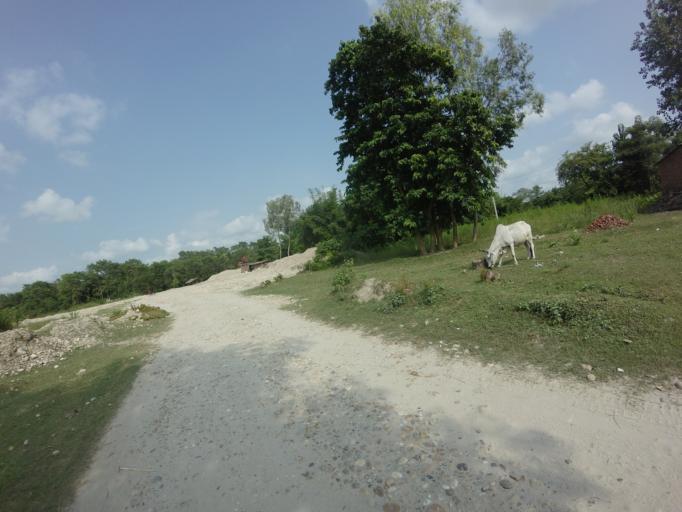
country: NP
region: Far Western
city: Tikapur
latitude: 28.4461
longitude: 81.0748
